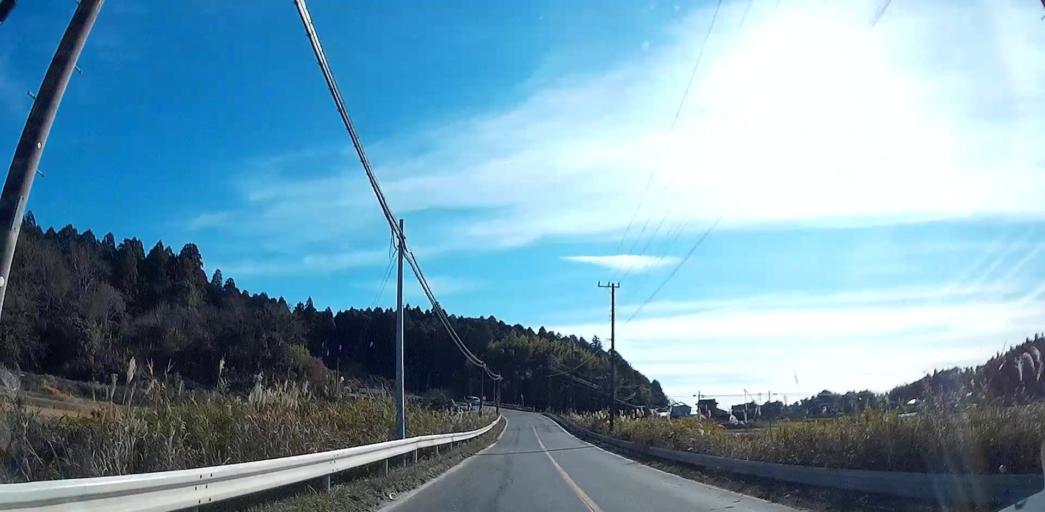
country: JP
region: Chiba
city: Yokaichiba
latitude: 35.7610
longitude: 140.4504
